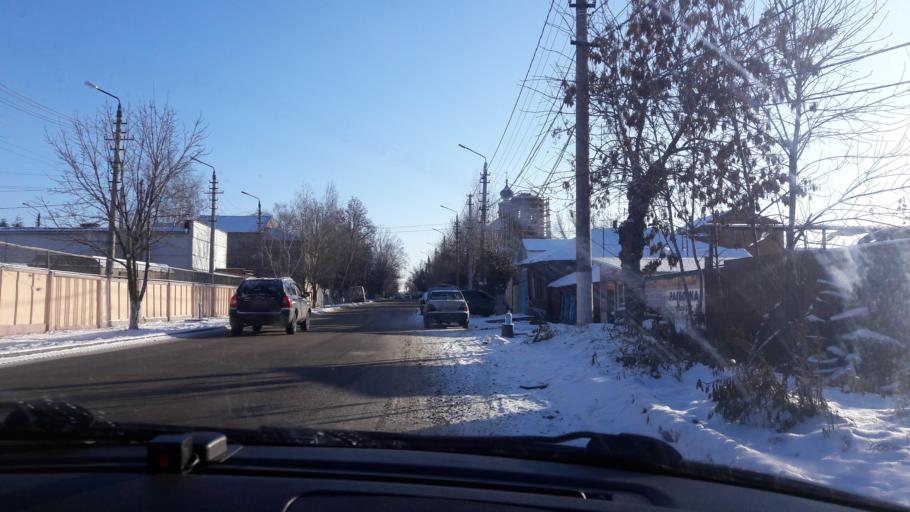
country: RU
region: Tula
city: Tula
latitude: 54.1995
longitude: 37.6289
